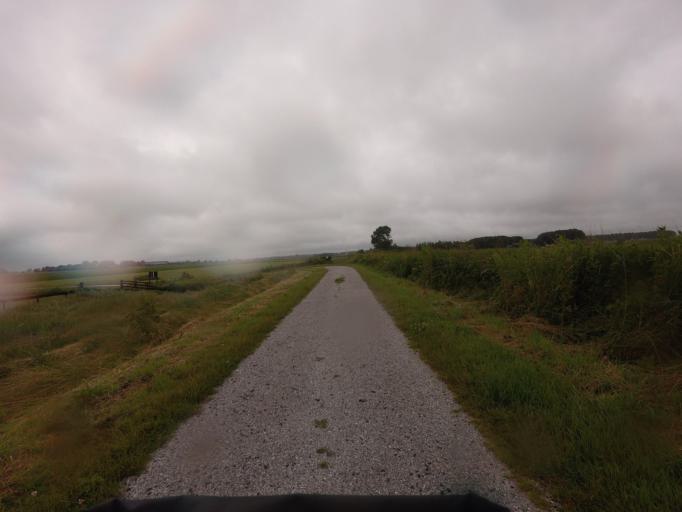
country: NL
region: North Holland
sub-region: Gemeente Opmeer
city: Opmeer
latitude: 52.7498
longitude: 4.9386
